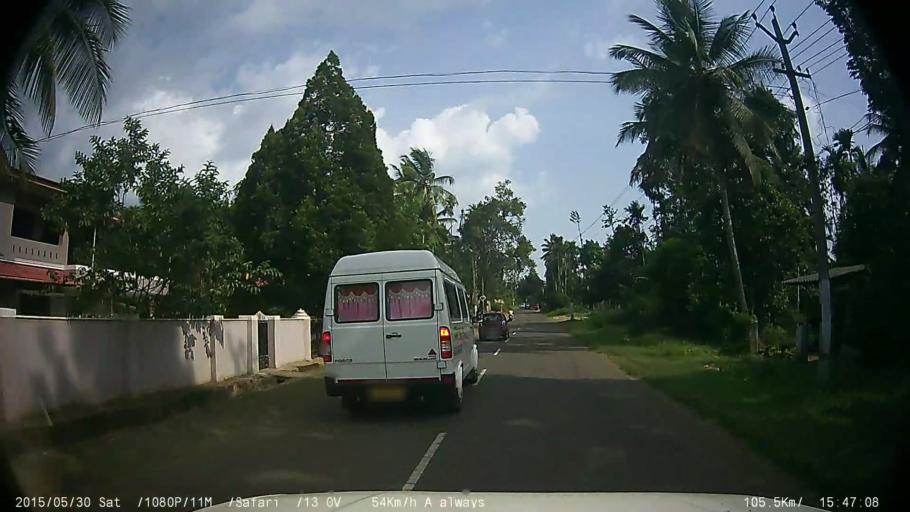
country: IN
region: Kerala
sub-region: Wayanad
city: Panamaram
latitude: 11.7062
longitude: 76.0784
